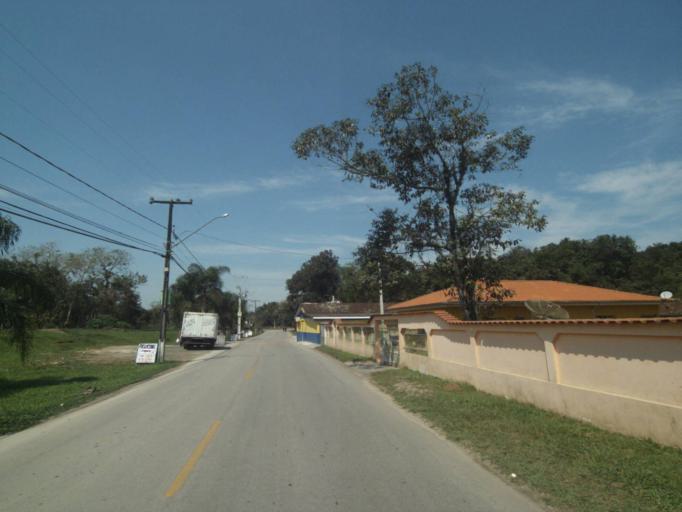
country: BR
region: Parana
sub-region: Paranagua
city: Paranagua
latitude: -25.5589
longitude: -48.6267
